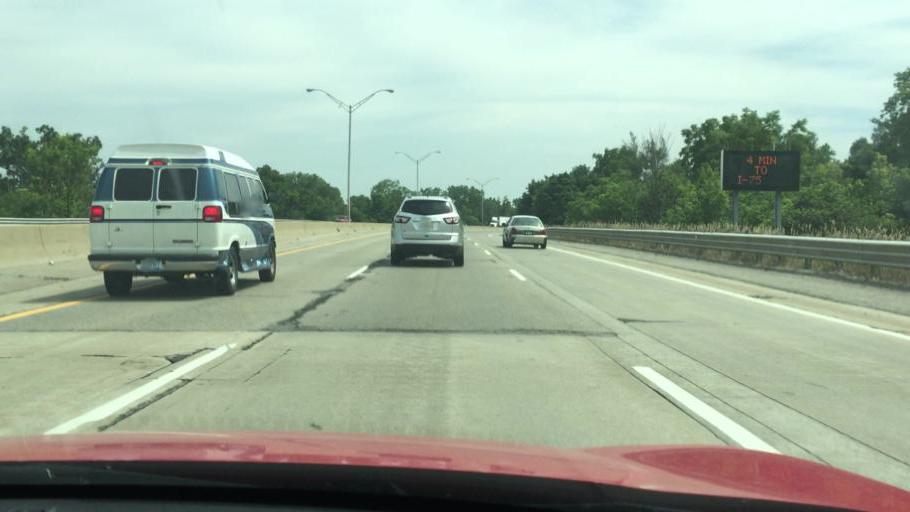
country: US
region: Michigan
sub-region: Genesee County
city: Flint
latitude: 43.0014
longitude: -83.6758
